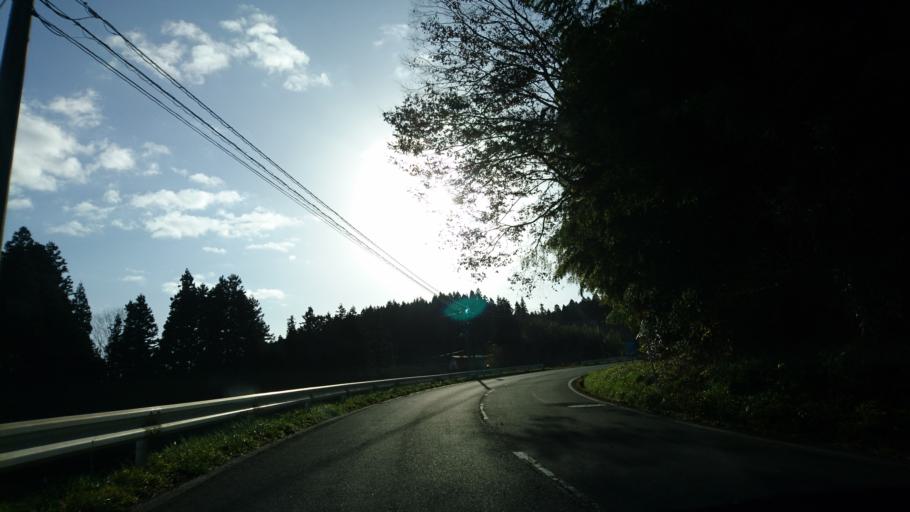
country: JP
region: Iwate
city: Ichinoseki
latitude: 38.8920
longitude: 141.2863
